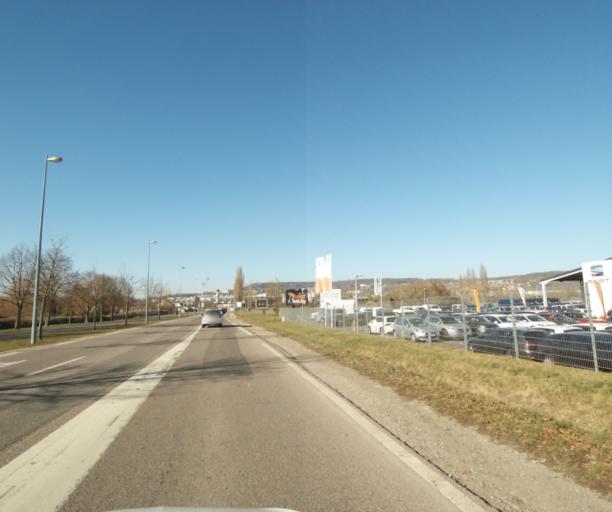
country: FR
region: Lorraine
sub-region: Departement de Meurthe-et-Moselle
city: Tomblaine
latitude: 48.6900
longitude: 6.2150
